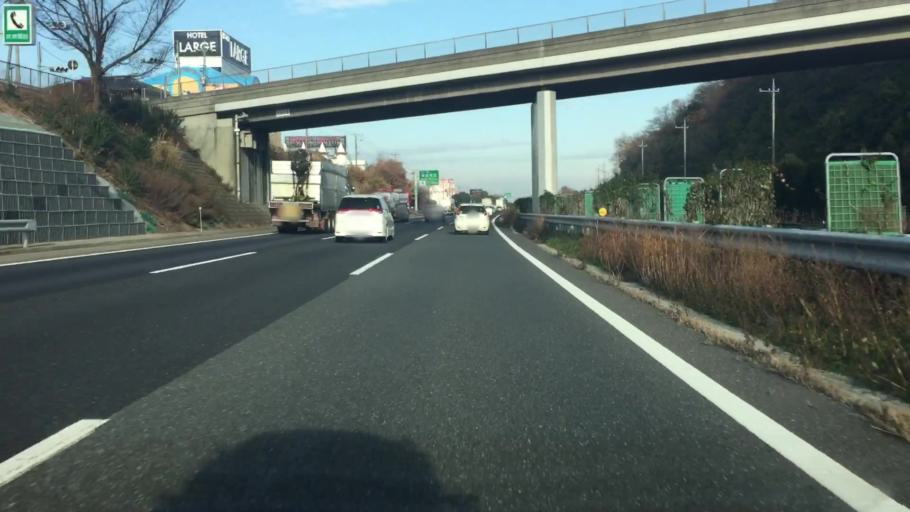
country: JP
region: Saitama
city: Honjo
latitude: 36.2109
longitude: 139.1694
